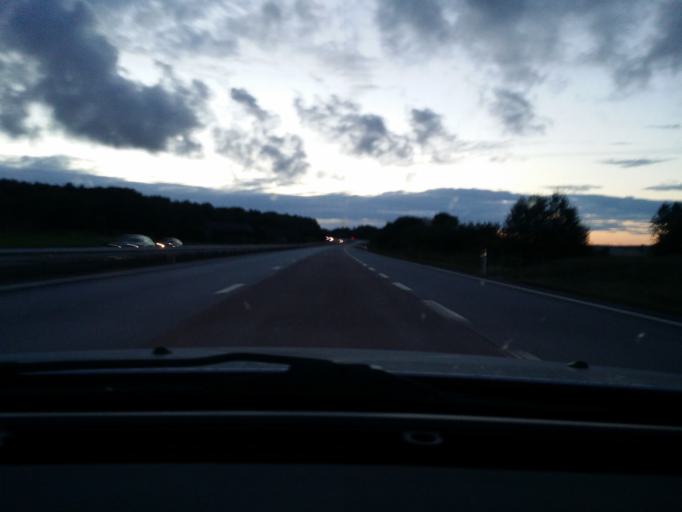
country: SE
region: Uppsala
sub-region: Habo Kommun
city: Balsta
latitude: 59.5866
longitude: 17.5068
